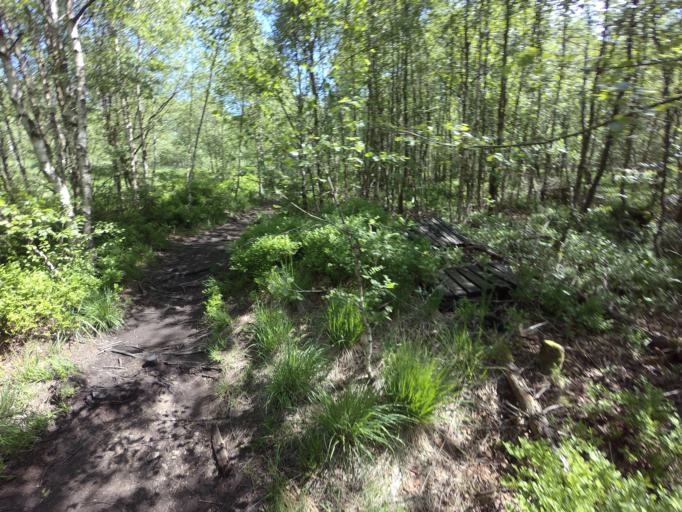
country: BE
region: Wallonia
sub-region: Province de Liege
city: Malmedy
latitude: 50.5035
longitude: 6.0650
